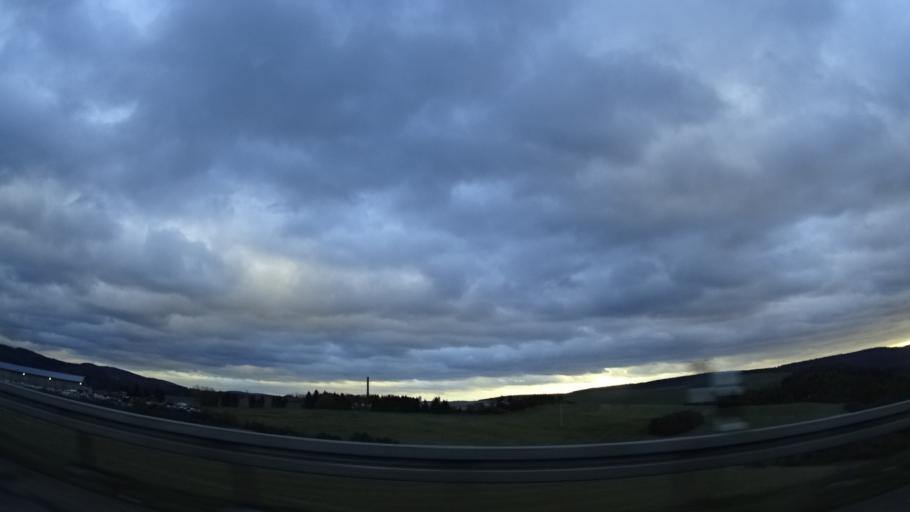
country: DE
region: Thuringia
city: Dillstadt
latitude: 50.5976
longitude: 10.5271
